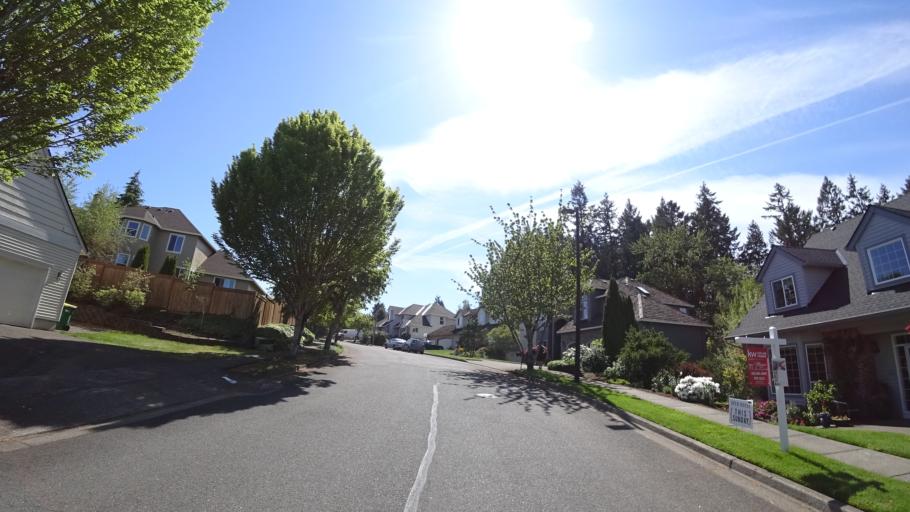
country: US
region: Oregon
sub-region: Washington County
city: Aloha
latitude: 45.4511
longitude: -122.8423
